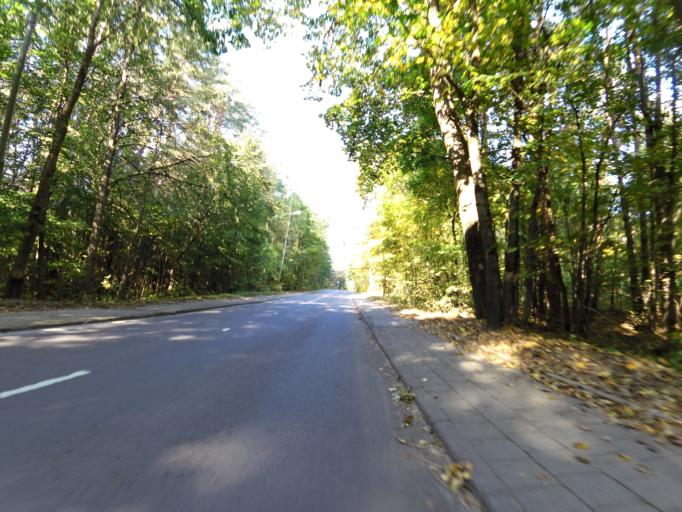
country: LT
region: Vilnius County
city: Rasos
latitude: 54.7297
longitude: 25.3115
